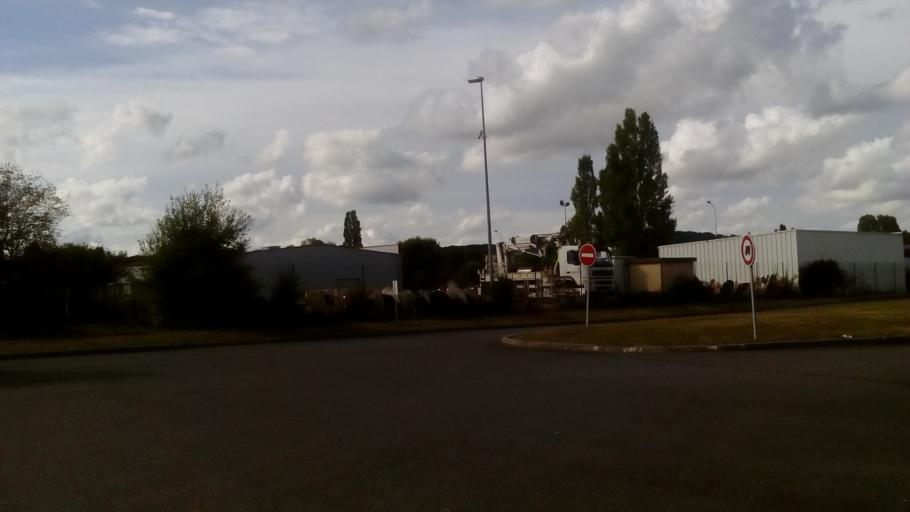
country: FR
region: Bourgogne
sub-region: Departement de la Nievre
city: Varennes-Vauzelles
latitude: 47.0450
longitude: 3.1308
